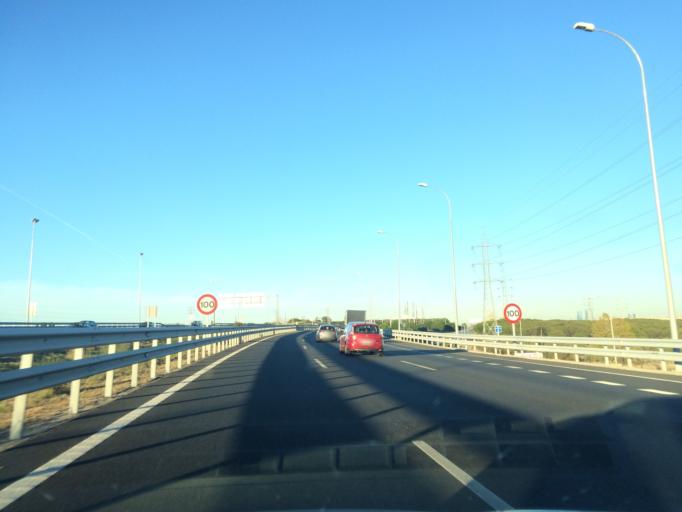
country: ES
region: Madrid
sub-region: Provincia de Madrid
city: Pozuelo de Alarcon
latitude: 40.4048
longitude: -3.8293
